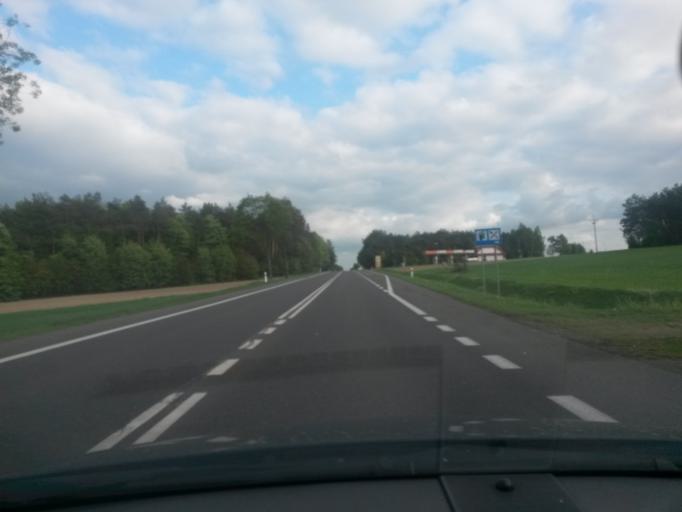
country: PL
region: Masovian Voivodeship
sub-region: Powiat plocki
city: Starozreby
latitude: 52.6669
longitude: 20.0728
